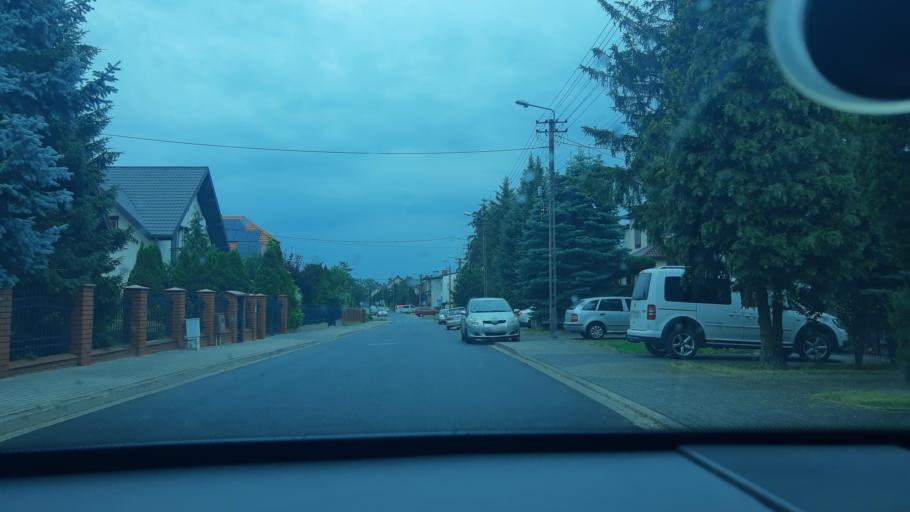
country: PL
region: Lodz Voivodeship
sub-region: Powiat sieradzki
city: Sieradz
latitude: 51.5757
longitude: 18.7398
